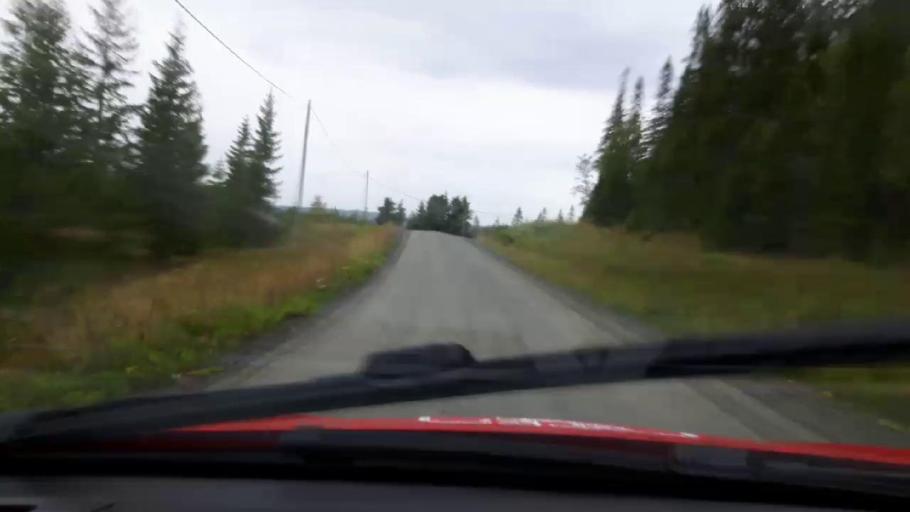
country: SE
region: Jaemtland
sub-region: Are Kommun
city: Are
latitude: 63.4189
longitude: 12.8253
